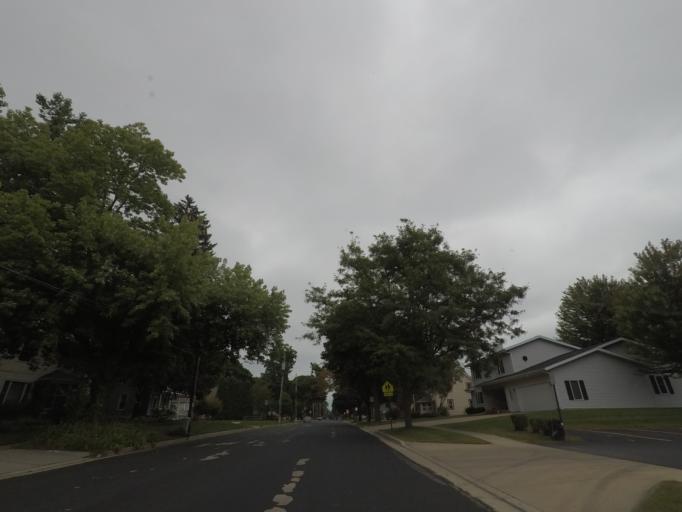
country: US
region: Wisconsin
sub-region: Dane County
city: Middleton
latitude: 43.0982
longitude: -89.5099
